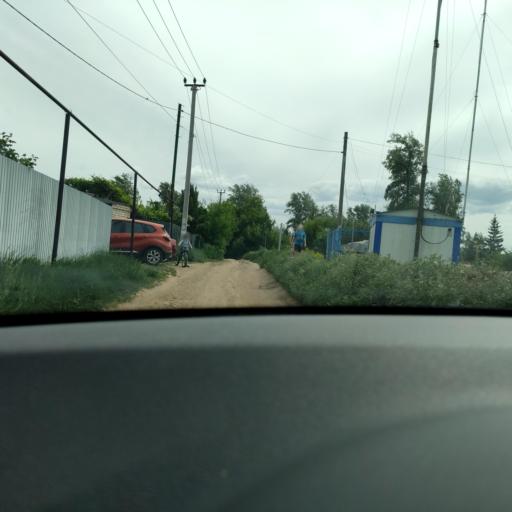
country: RU
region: Samara
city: Novokuybyshevsk
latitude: 53.1503
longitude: 50.0165
